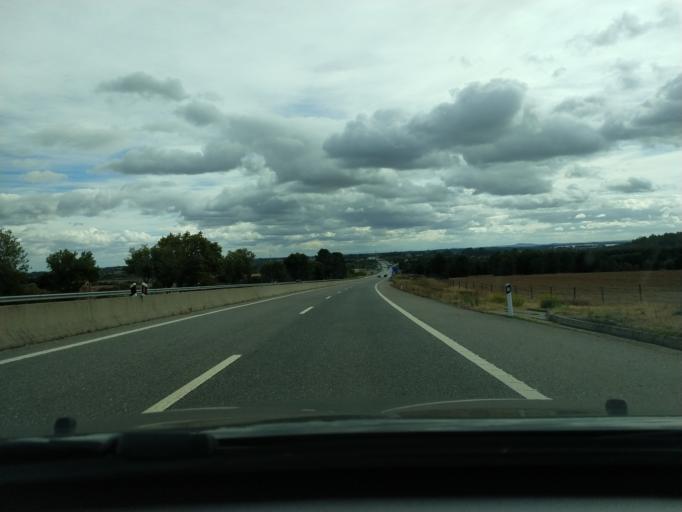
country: PT
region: Castelo Branco
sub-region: Concelho do Fundao
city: Fundao
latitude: 40.0426
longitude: -7.4703
